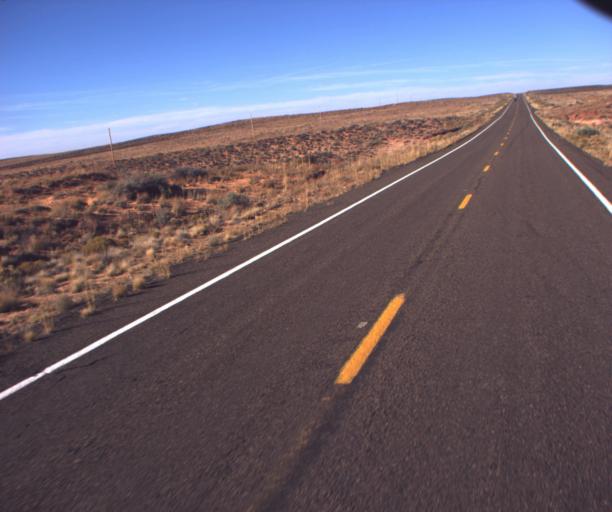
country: US
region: Arizona
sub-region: Coconino County
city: LeChee
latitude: 36.7620
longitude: -111.2851
